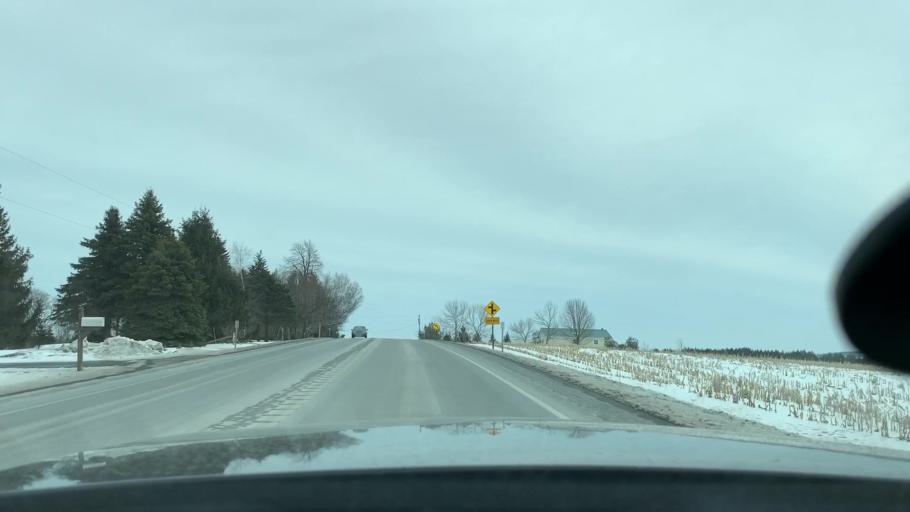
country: US
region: New York
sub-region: Oneida County
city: Utica
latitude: 43.0314
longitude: -75.1744
